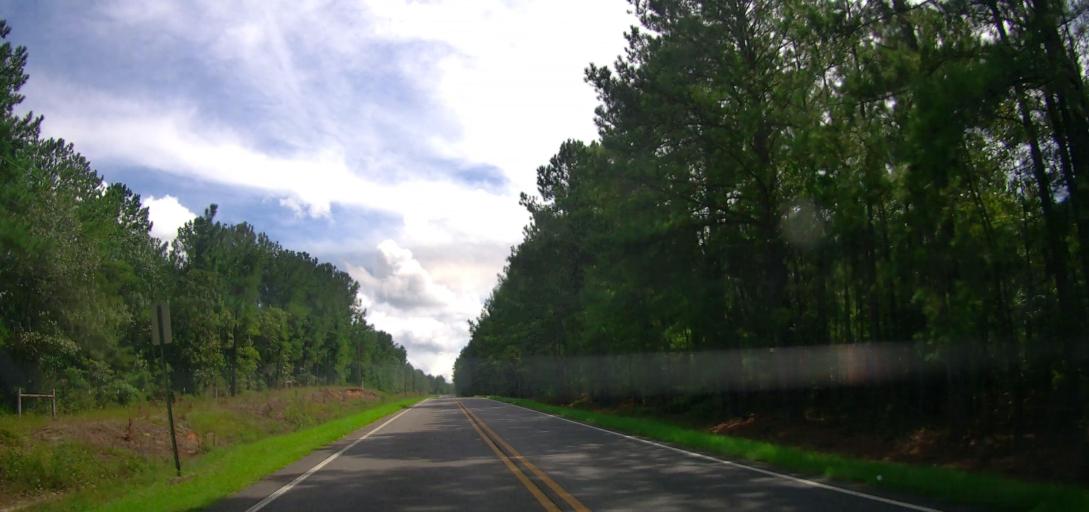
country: US
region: Georgia
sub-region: Taylor County
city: Butler
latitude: 32.5284
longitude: -84.2082
